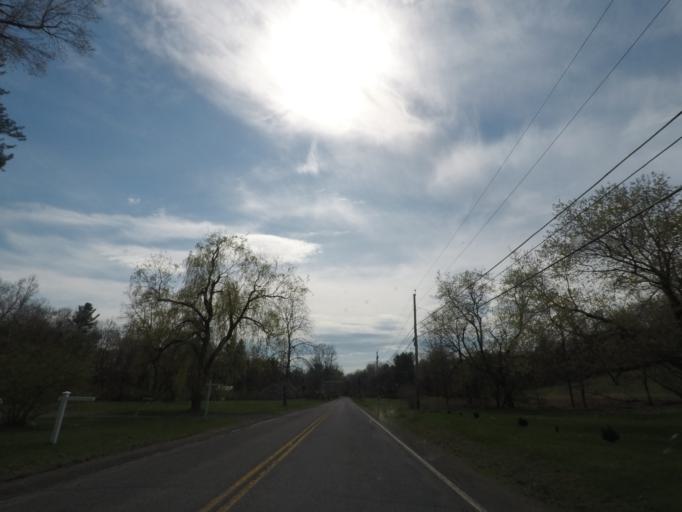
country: US
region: New York
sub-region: Columbia County
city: Chatham
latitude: 42.3542
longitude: -73.5578
